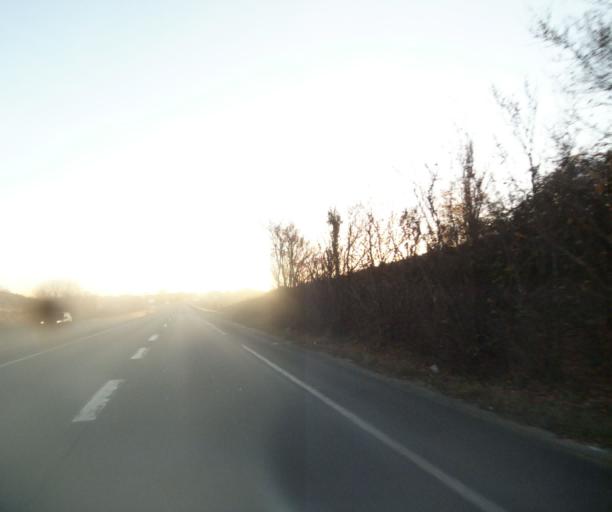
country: FR
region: Poitou-Charentes
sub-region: Departement de la Charente-Maritime
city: Saintes
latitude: 45.7253
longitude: -0.6452
